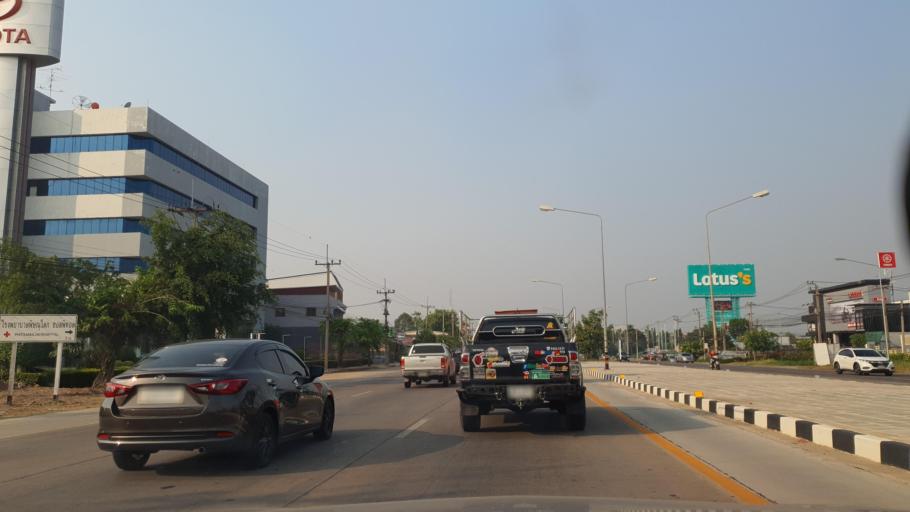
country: TH
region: Phitsanulok
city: Phitsanulok
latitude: 16.7981
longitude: 100.2131
